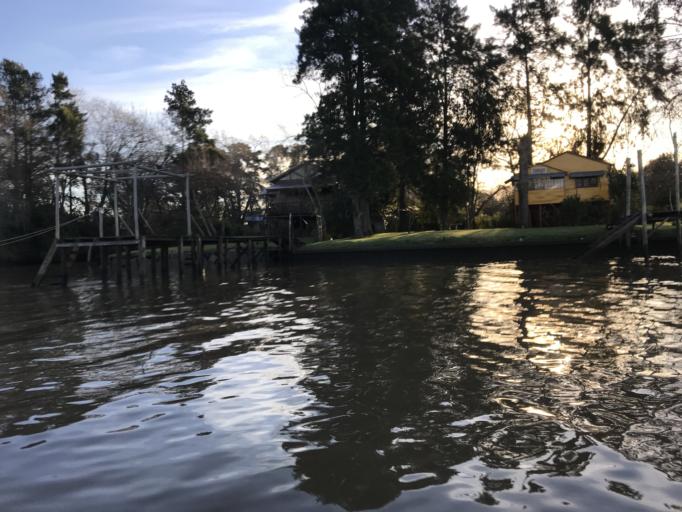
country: AR
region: Buenos Aires
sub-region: Partido de Tigre
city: Tigre
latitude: -34.3857
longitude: -58.5777
